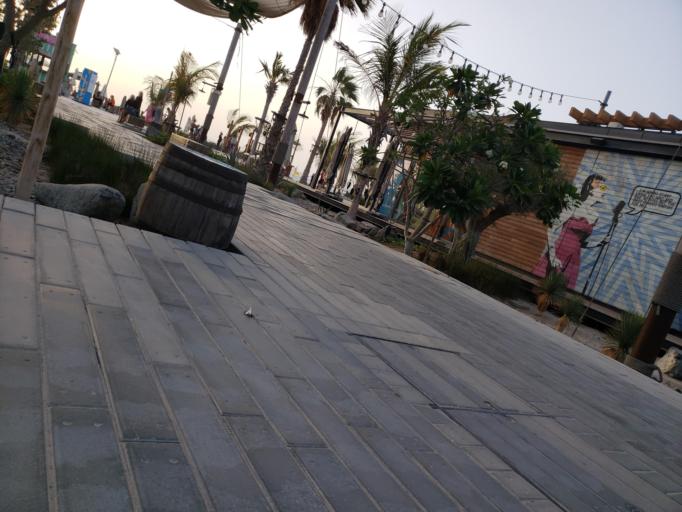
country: AE
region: Dubai
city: Dubai
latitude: 25.2264
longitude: 55.2567
